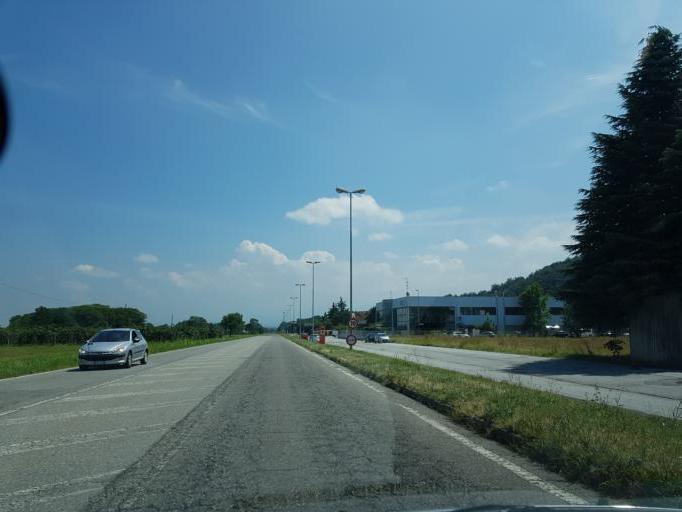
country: IT
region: Piedmont
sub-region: Provincia di Cuneo
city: Montemale di Cuneo
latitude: 44.4487
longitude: 7.3960
